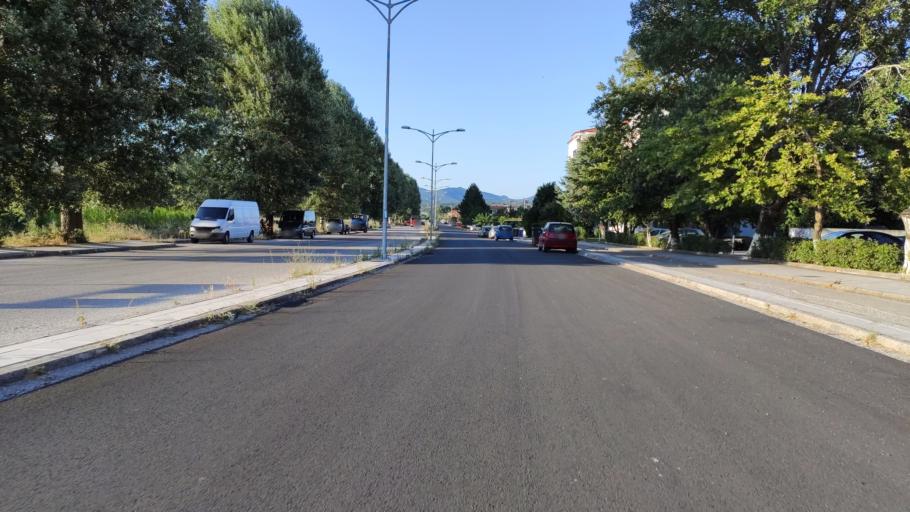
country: GR
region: East Macedonia and Thrace
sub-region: Nomos Rodopis
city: Komotini
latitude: 41.1261
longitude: 25.3936
